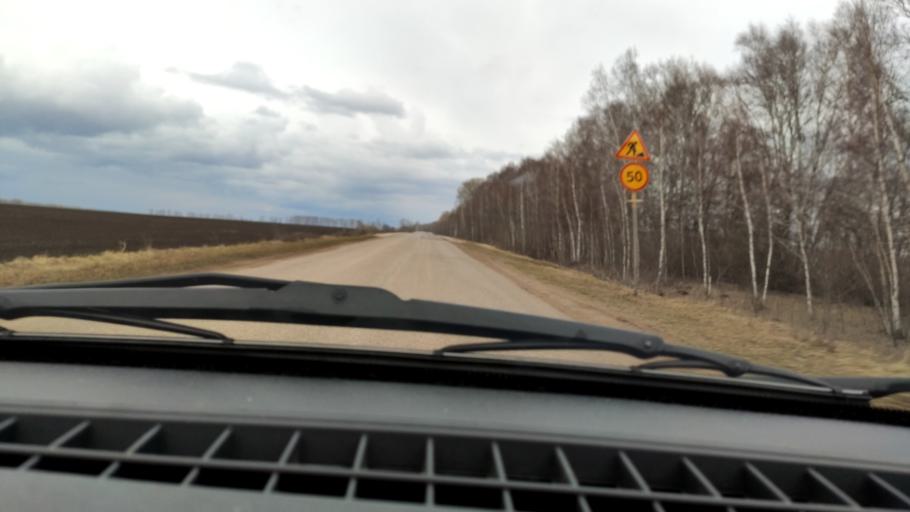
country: RU
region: Bashkortostan
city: Semiletka
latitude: 55.2529
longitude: 54.6169
